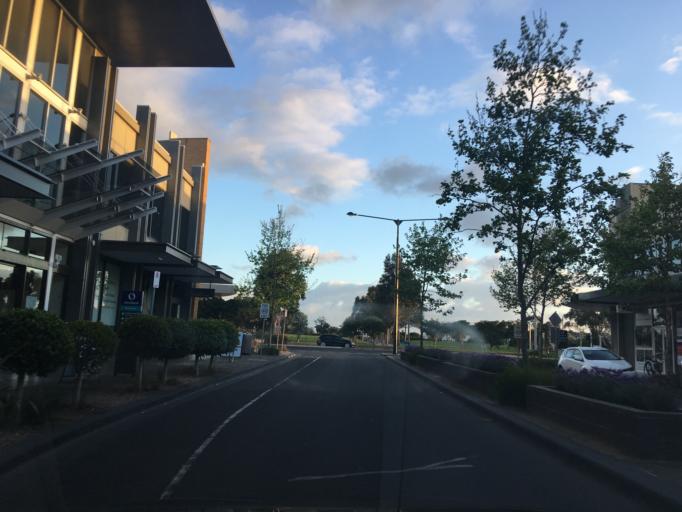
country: AU
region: Victoria
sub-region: Wyndham
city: Williams Landing
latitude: -37.8843
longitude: 144.7352
